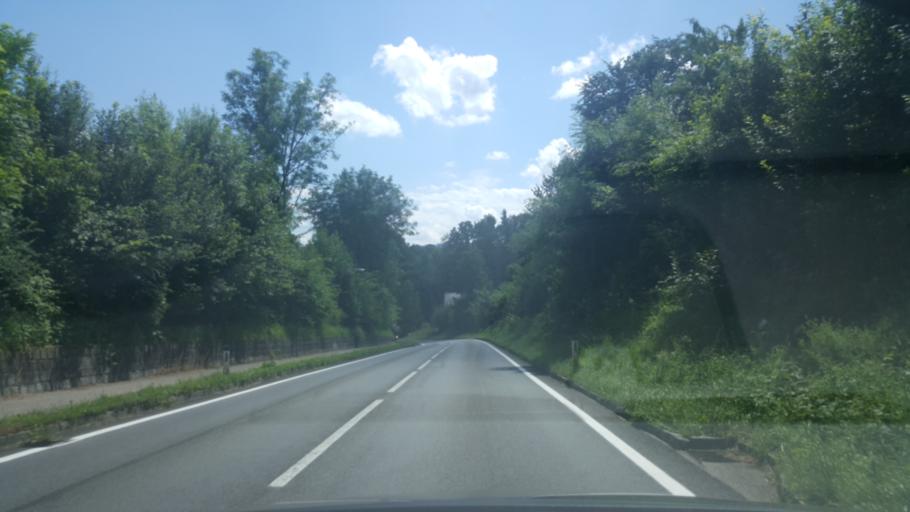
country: AT
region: Upper Austria
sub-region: Politischer Bezirk Vocklabruck
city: Gampern
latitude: 47.9995
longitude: 13.5451
